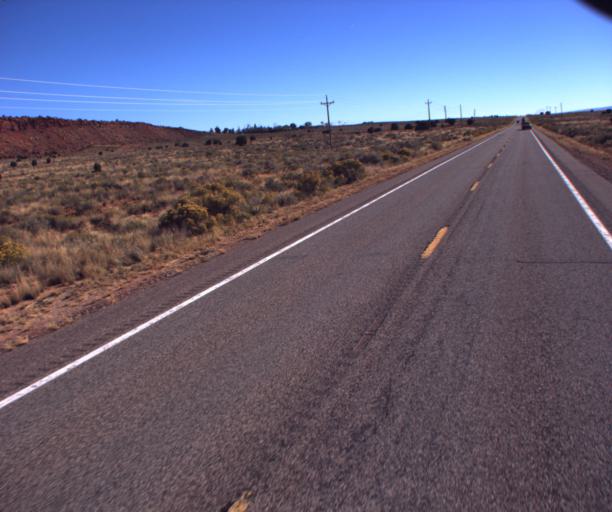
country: US
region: Arizona
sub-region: Coconino County
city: Fredonia
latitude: 36.8578
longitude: -112.7530
